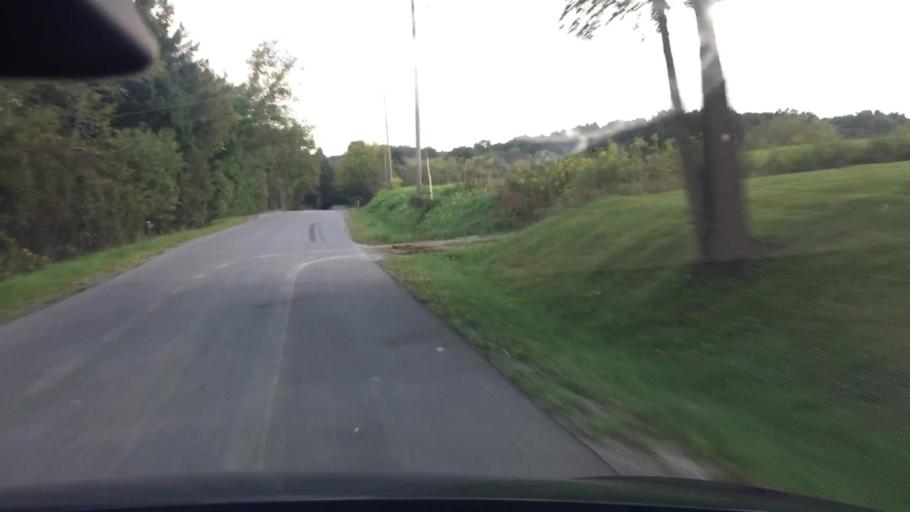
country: US
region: Pennsylvania
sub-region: Butler County
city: Oak Hills
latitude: 40.8011
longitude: -79.8871
